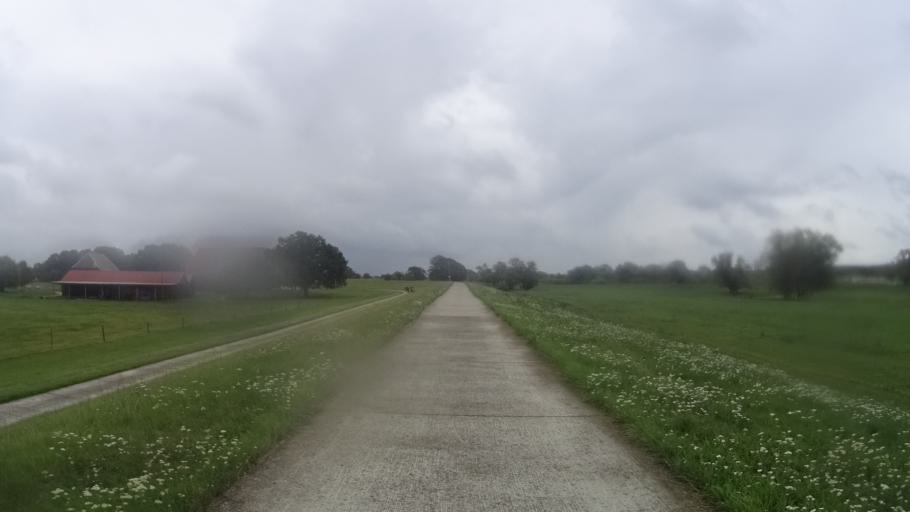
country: DE
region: Lower Saxony
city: Bleckede
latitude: 53.2991
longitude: 10.7483
